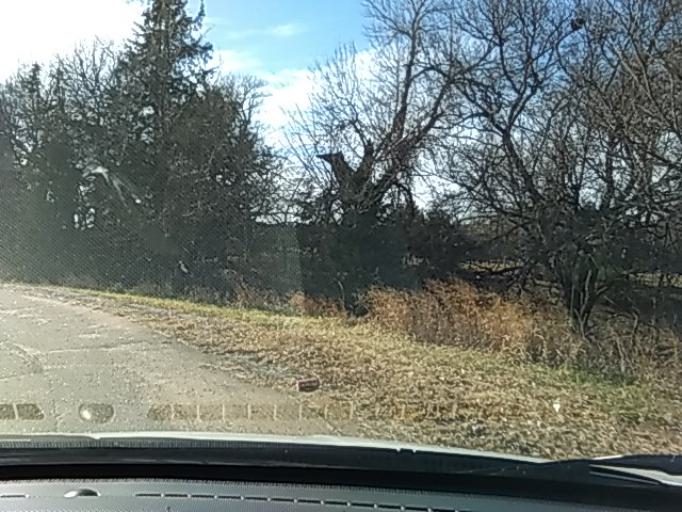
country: US
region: Nebraska
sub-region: Nuckolls County
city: Nelson
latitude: 40.3314
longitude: -98.0675
